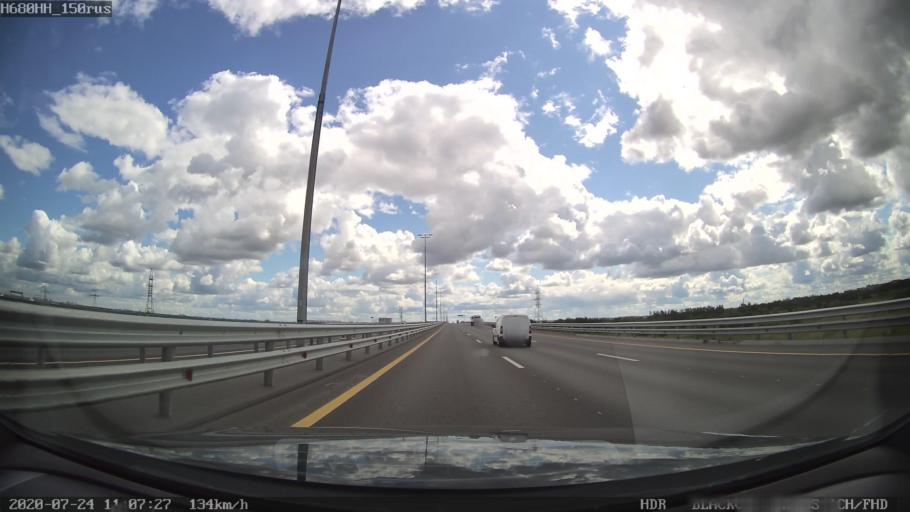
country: RU
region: St.-Petersburg
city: Pushkin
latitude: 59.7560
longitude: 30.4057
